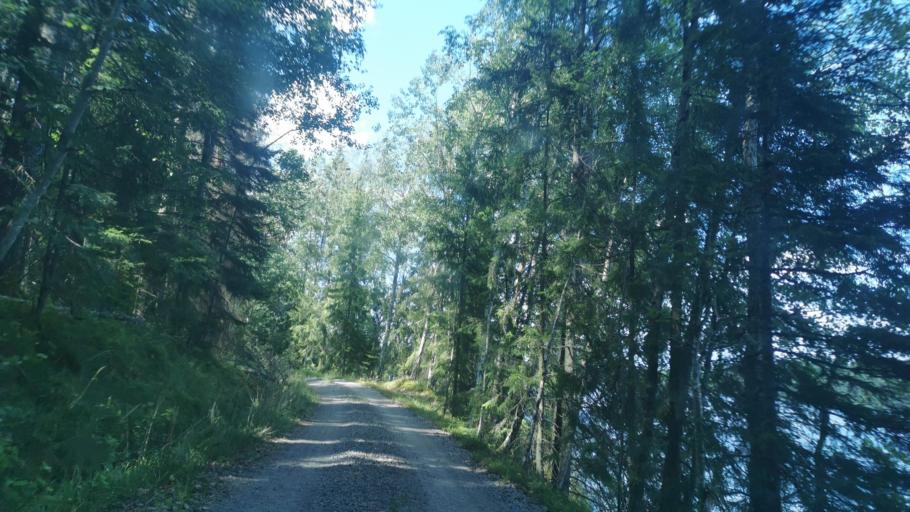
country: SE
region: OEstergoetland
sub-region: Finspangs Kommun
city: Finspang
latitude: 58.7960
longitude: 15.8210
